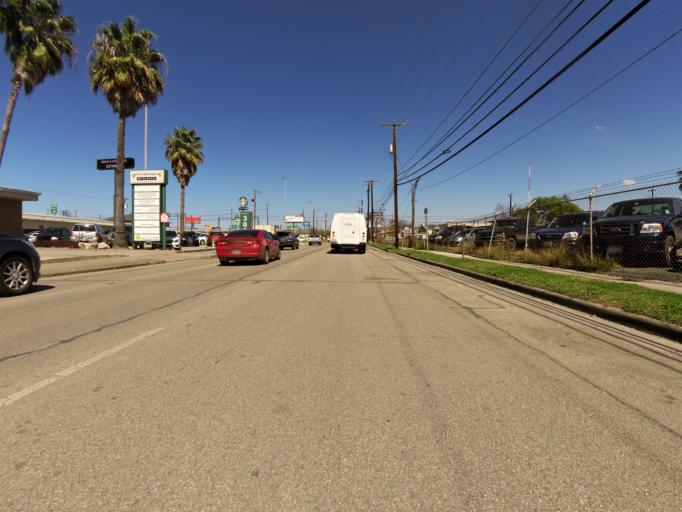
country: US
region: Texas
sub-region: Bexar County
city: San Antonio
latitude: 29.4360
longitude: -98.4919
